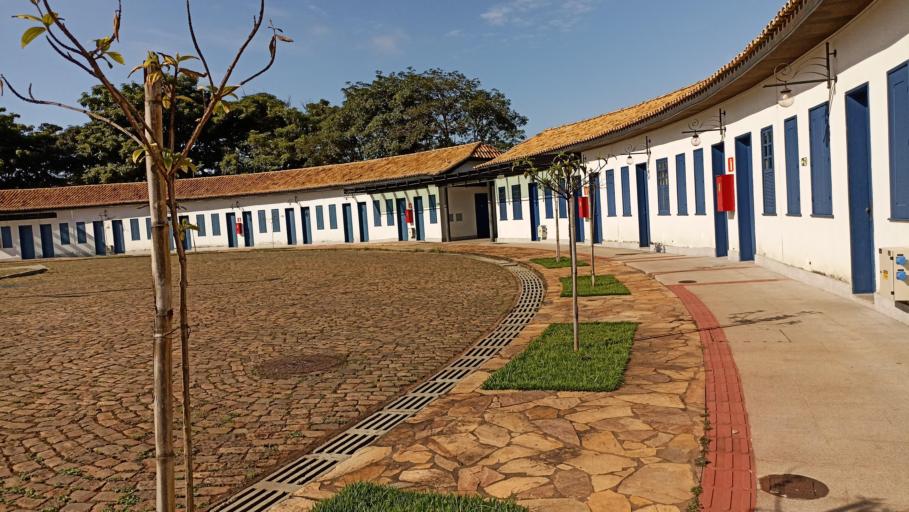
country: BR
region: Minas Gerais
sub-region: Congonhas
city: Congonhas
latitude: -20.5064
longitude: -43.8631
